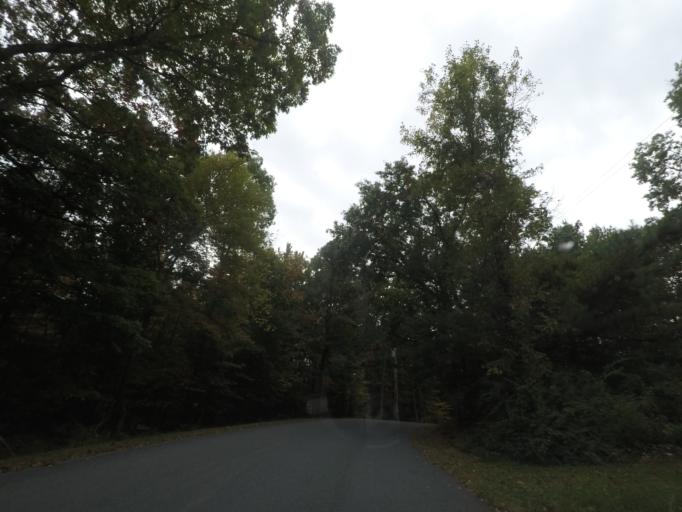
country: US
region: New York
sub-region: Rensselaer County
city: Nassau
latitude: 42.5434
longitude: -73.6460
